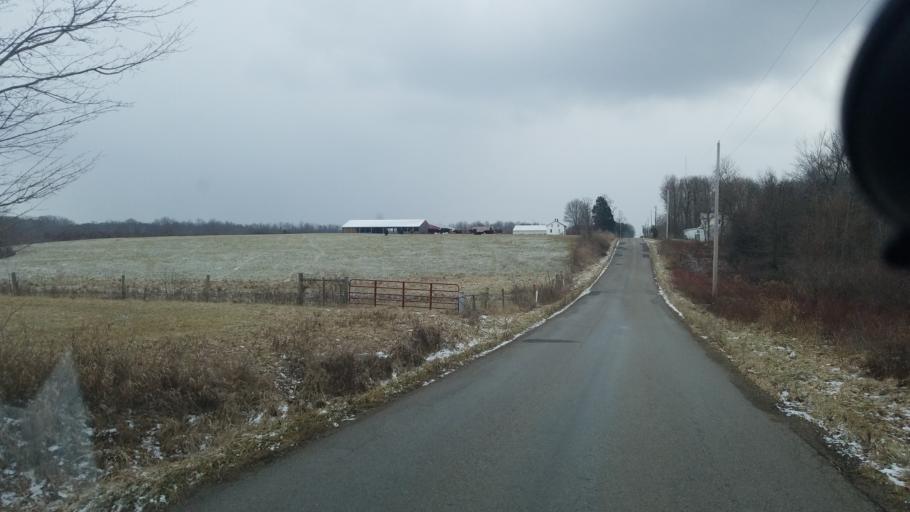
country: US
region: Ohio
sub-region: Morrow County
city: Mount Gilead
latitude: 40.5953
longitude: -82.8048
